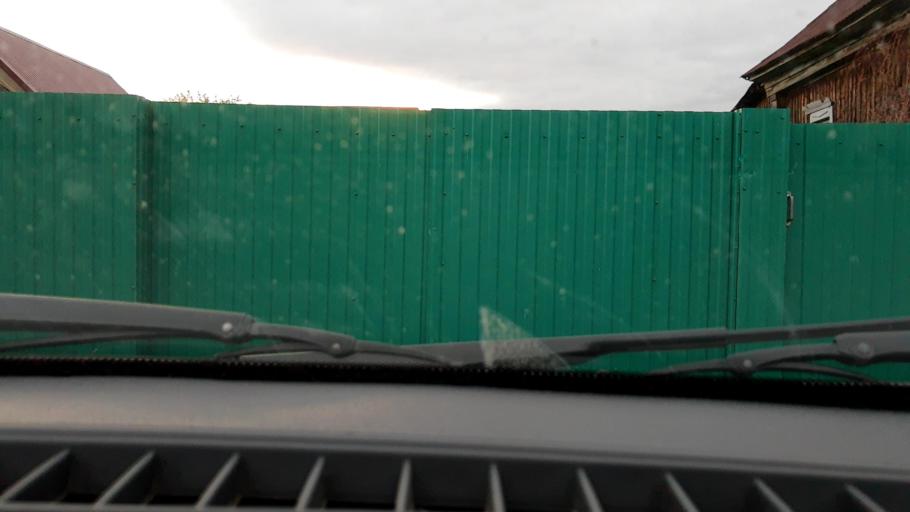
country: RU
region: Bashkortostan
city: Ulukulevo
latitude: 54.3843
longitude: 56.3796
